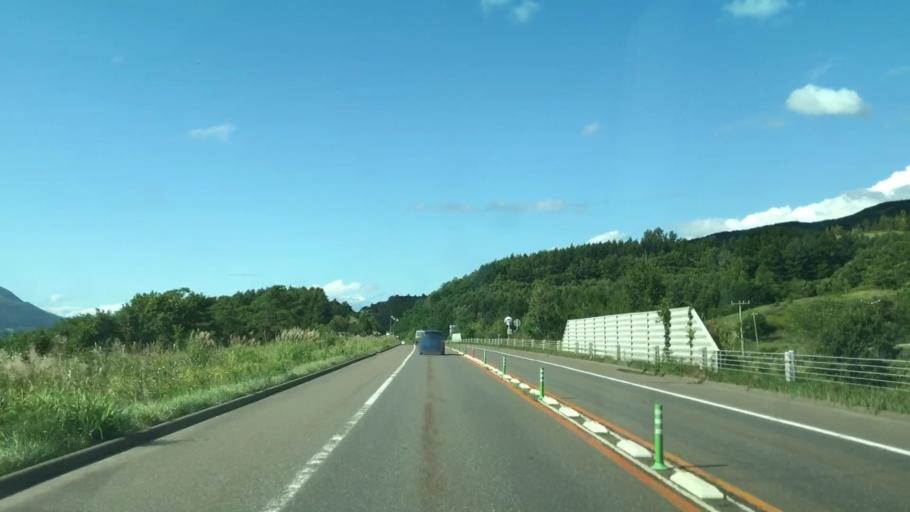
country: JP
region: Hokkaido
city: Date
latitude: 42.4522
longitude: 140.9132
